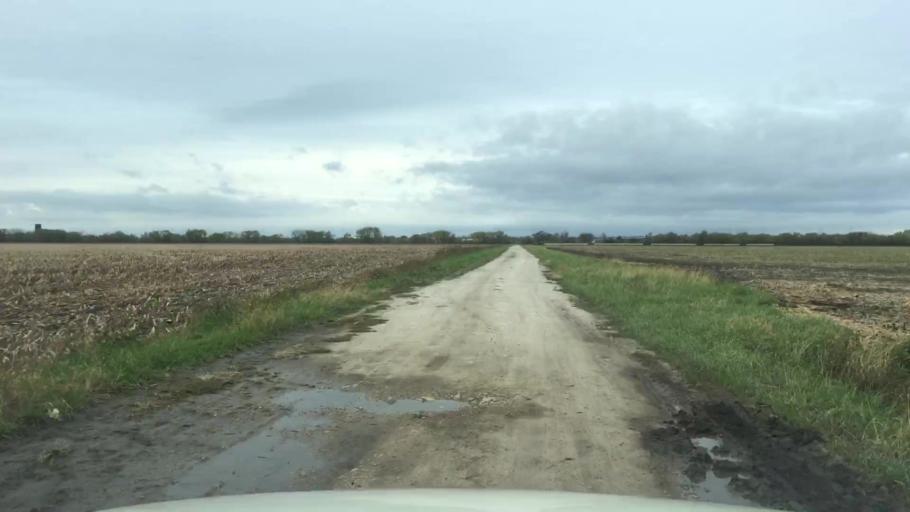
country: US
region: Kansas
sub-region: Douglas County
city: Eudora
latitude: 38.9315
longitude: -95.1491
